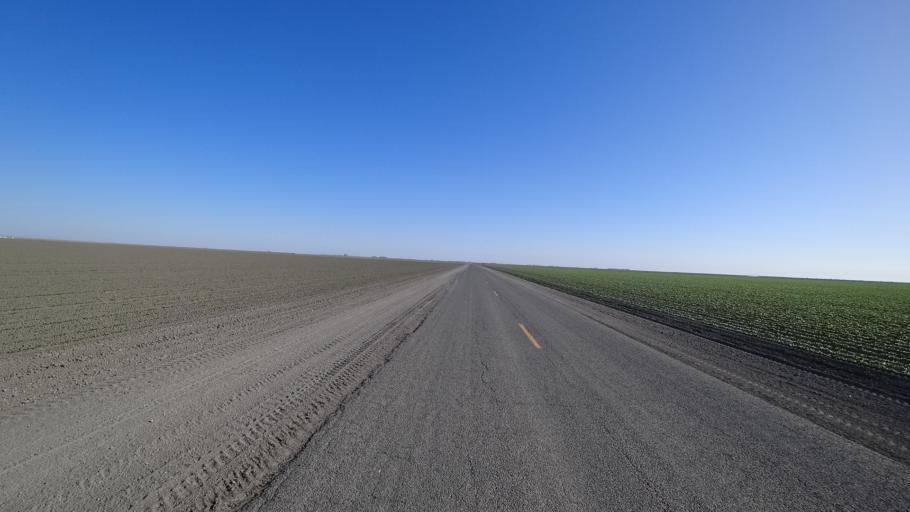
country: US
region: California
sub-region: Kings County
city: Stratford
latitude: 36.1043
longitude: -119.7979
